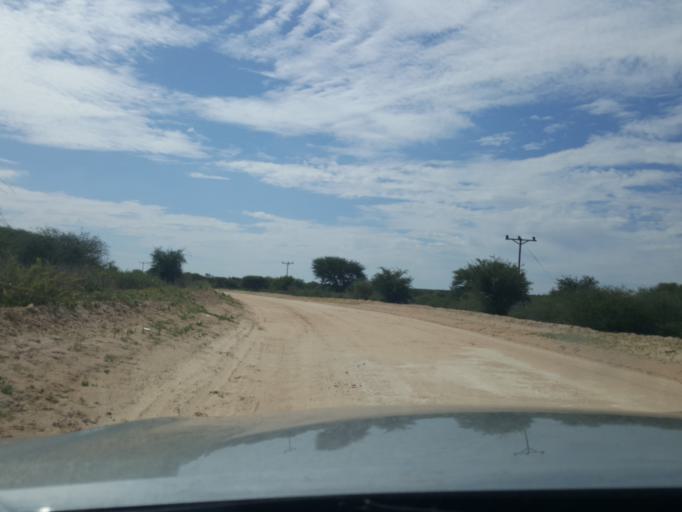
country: BW
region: Kweneng
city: Letlhakeng
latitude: -24.0556
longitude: 25.0307
